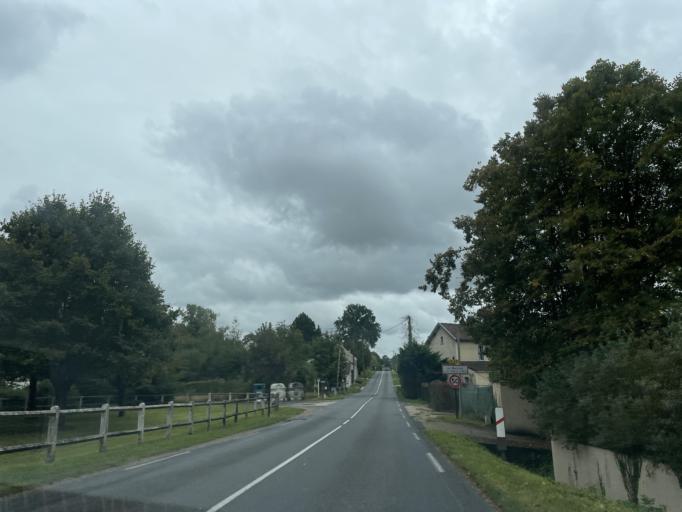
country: FR
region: Ile-de-France
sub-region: Departement de Seine-et-Marne
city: Boissy-le-Chatel
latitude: 48.8138
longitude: 3.1325
